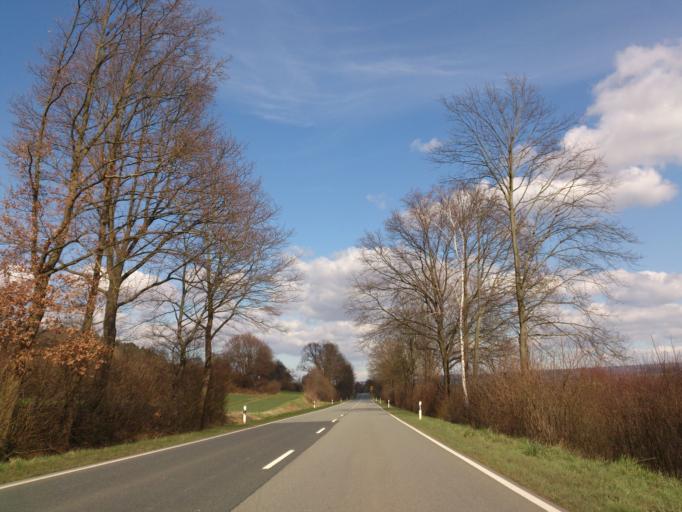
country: DE
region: Lower Saxony
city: Boffzen
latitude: 51.7175
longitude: 9.3306
